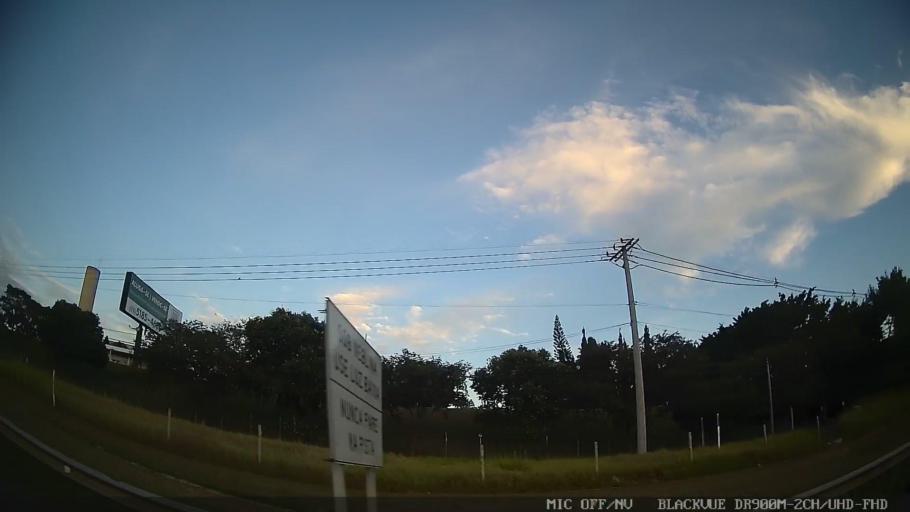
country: BR
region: Sao Paulo
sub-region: Indaiatuba
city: Indaiatuba
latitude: -23.1322
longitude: -47.2358
